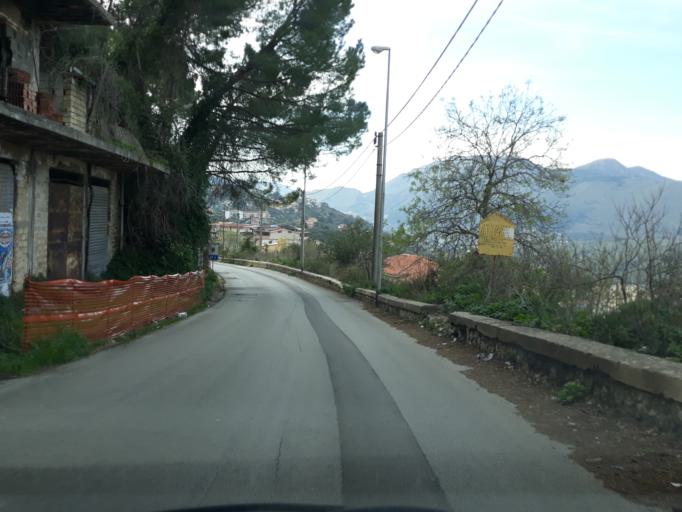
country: IT
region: Sicily
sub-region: Palermo
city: Altofonte
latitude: 38.0413
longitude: 13.2983
